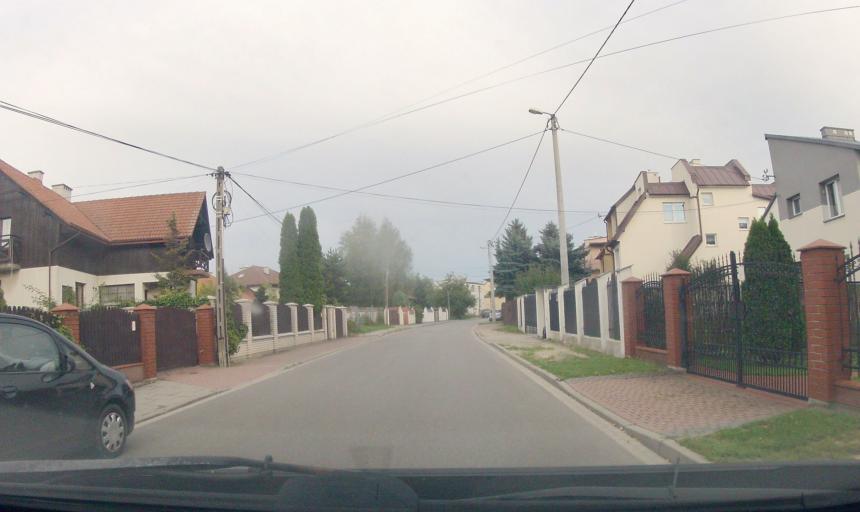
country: PL
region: Lesser Poland Voivodeship
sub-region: Krakow
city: Krakow
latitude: 50.0393
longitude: 19.9878
